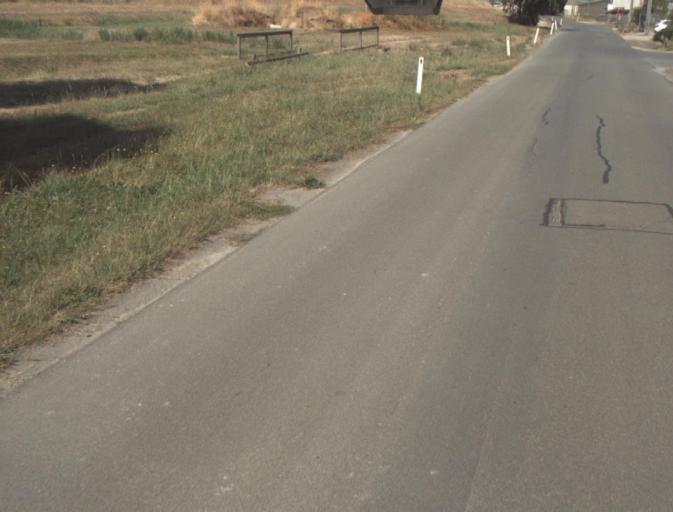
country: AU
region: Tasmania
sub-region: Launceston
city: East Launceston
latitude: -41.4188
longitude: 147.1430
